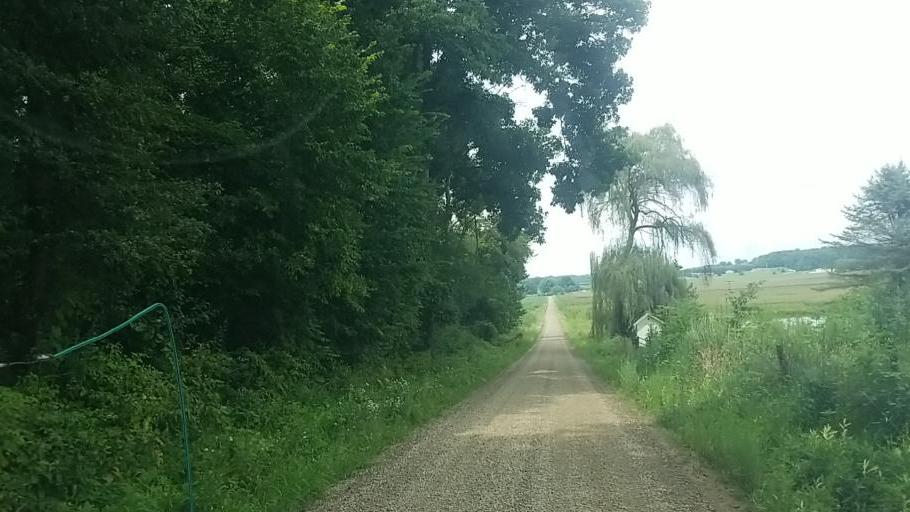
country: US
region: Ohio
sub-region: Knox County
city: Gambier
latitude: 40.3051
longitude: -82.3757
